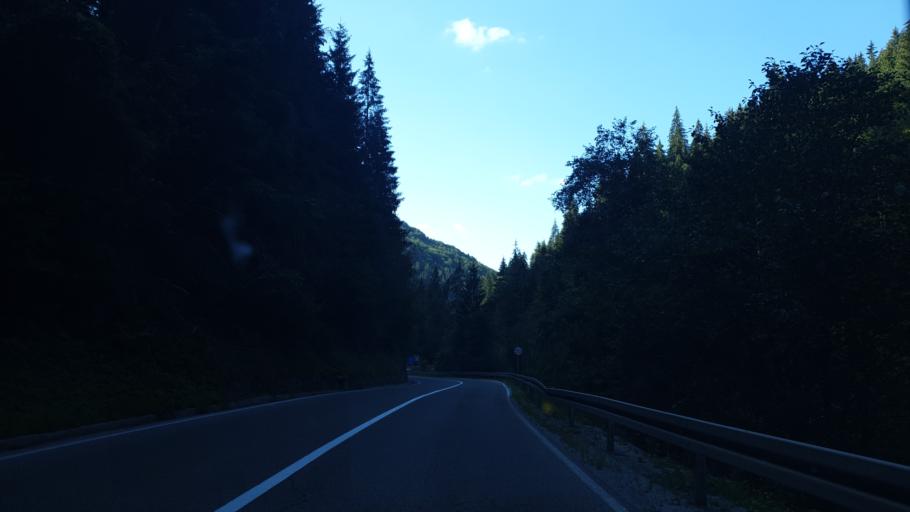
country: RS
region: Central Serbia
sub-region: Zlatiborski Okrug
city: Nova Varos
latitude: 43.4786
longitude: 19.8316
